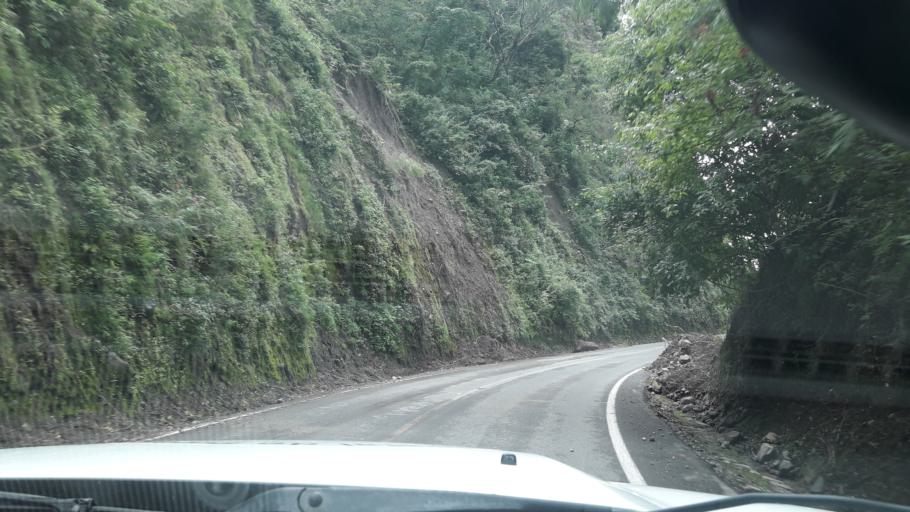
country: MX
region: Colima
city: Suchitlan
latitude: 19.4380
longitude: -103.7117
